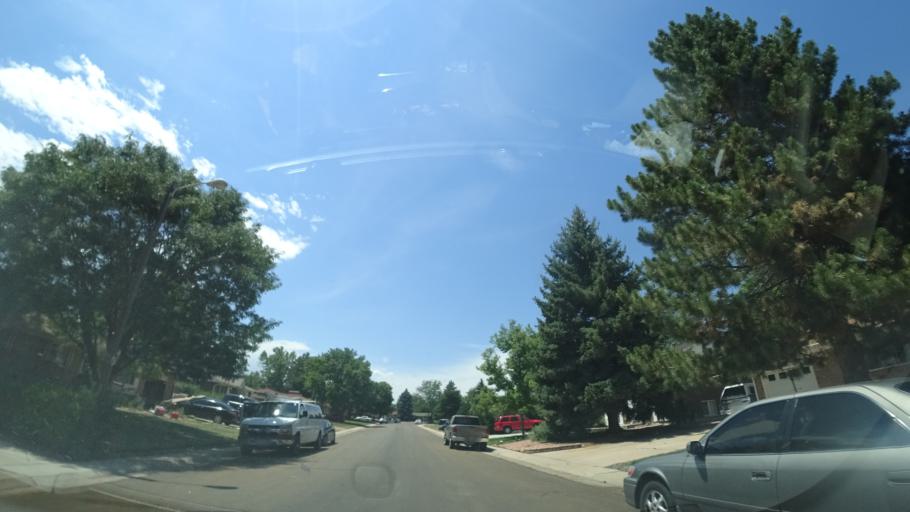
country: US
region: Colorado
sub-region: Jefferson County
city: Lakewood
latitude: 39.6926
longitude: -105.0877
